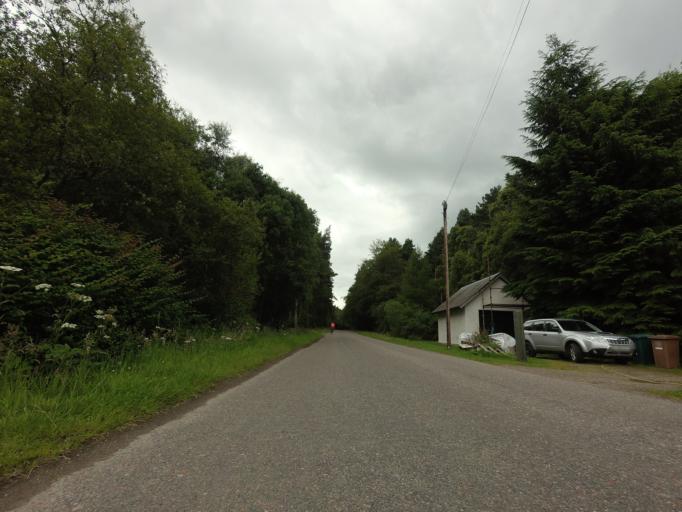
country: GB
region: Scotland
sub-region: Moray
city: Forres
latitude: 57.6201
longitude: -3.6746
